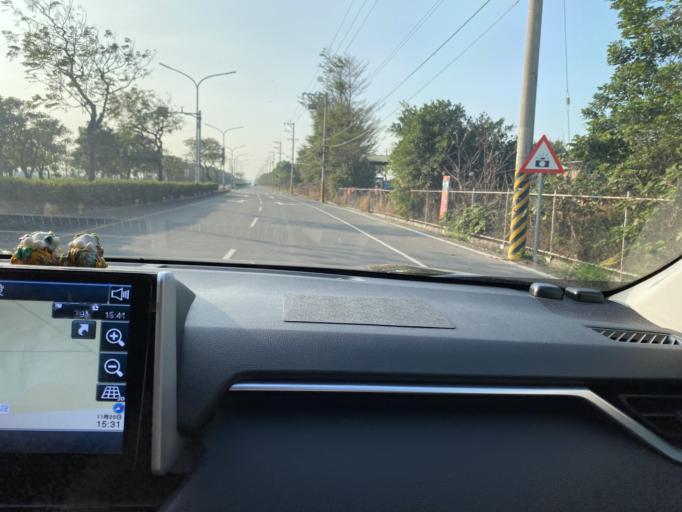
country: TW
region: Taiwan
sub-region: Changhua
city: Chang-hua
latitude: 23.9558
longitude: 120.4144
